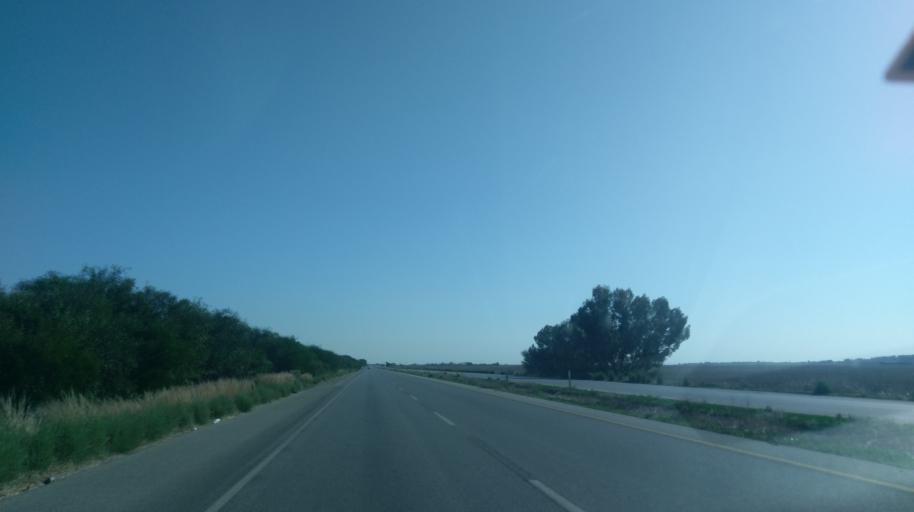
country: CY
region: Ammochostos
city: Lefkonoiko
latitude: 35.1853
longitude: 33.6666
